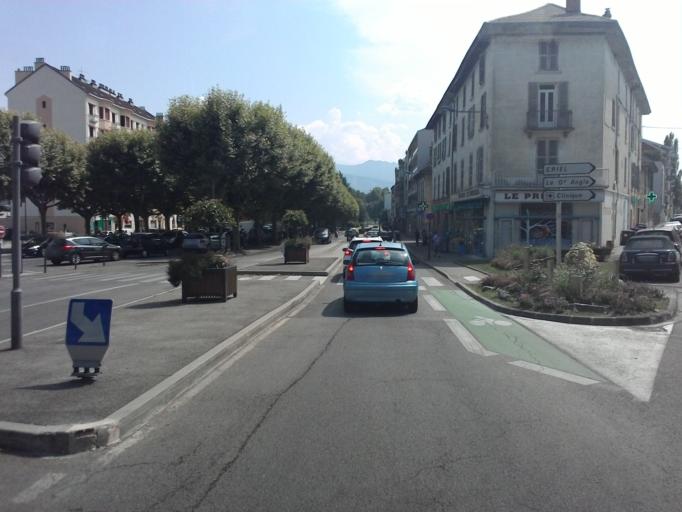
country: FR
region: Rhone-Alpes
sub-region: Departement de l'Isere
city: Voiron
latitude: 45.3650
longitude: 5.5909
